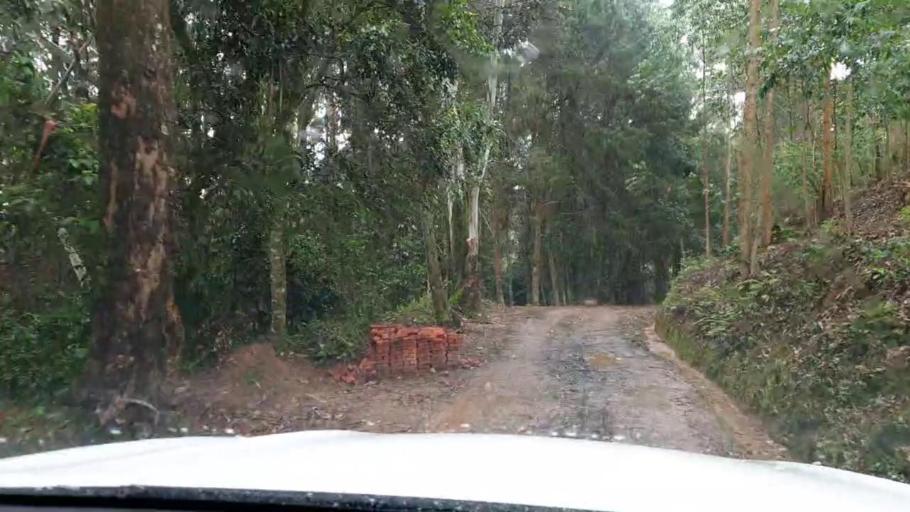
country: RW
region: Western Province
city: Cyangugu
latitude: -2.5546
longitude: 28.9779
